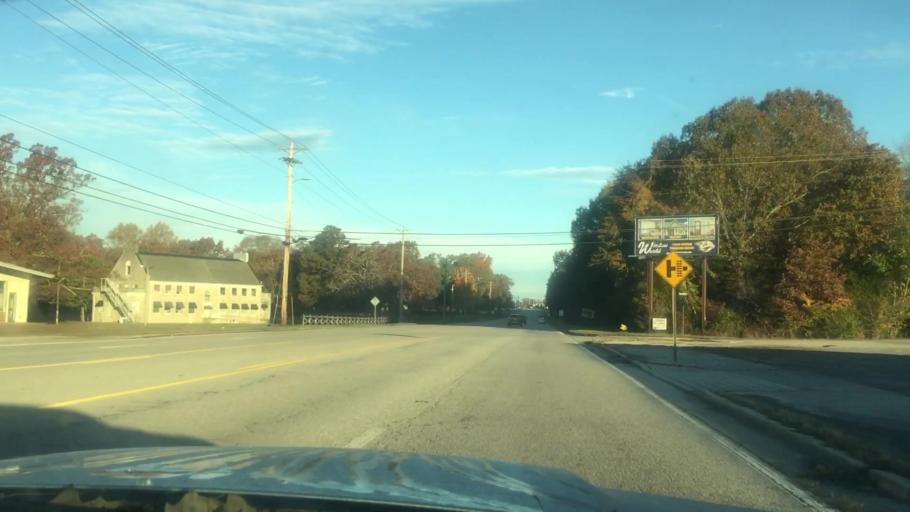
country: US
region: Tennessee
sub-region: Coffee County
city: Tullahoma
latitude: 35.3385
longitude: -86.1885
